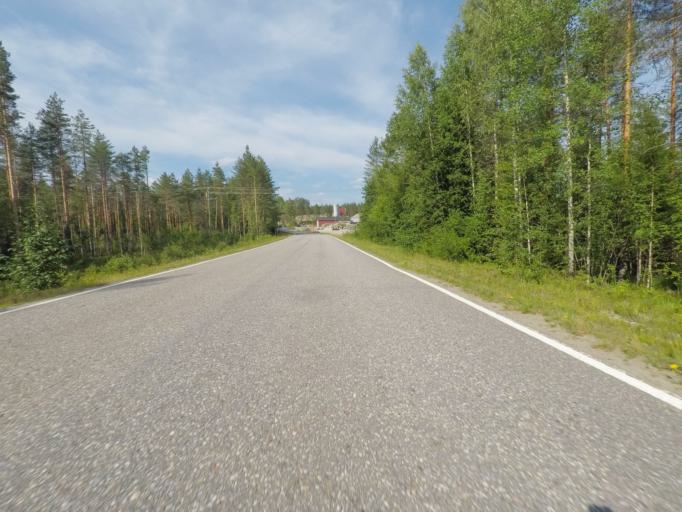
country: FI
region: Southern Savonia
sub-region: Savonlinna
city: Sulkava
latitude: 61.7853
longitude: 28.2422
